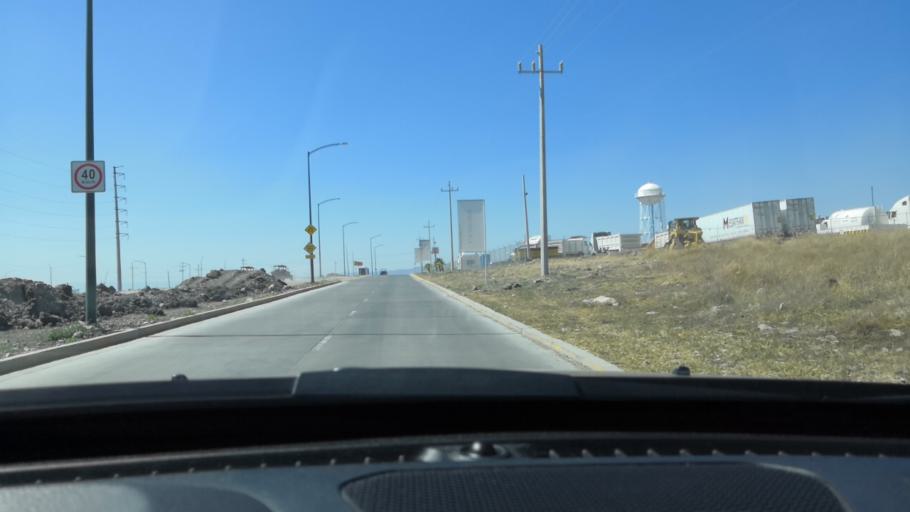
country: MX
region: Guanajuato
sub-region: Leon
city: Centro Familiar la Soledad
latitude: 21.1120
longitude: -101.7561
